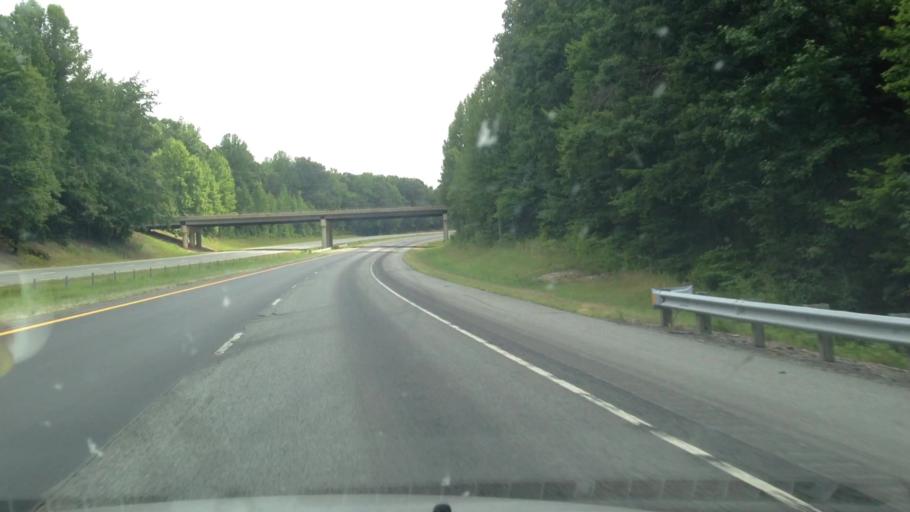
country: US
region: North Carolina
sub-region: Rockingham County
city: Reidsville
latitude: 36.4422
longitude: -79.5703
